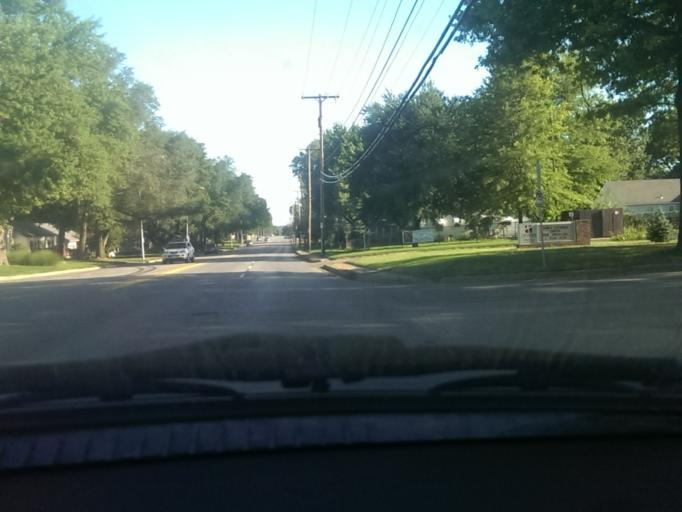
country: US
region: Kansas
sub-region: Johnson County
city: Leawood
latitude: 38.9737
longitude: -94.5952
